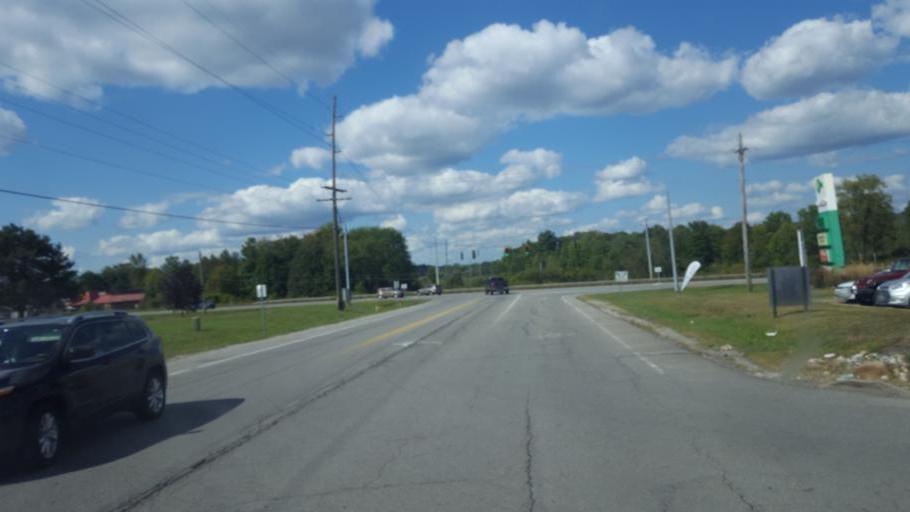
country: US
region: Ohio
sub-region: Ashland County
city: Ashland
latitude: 40.8566
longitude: -82.2631
